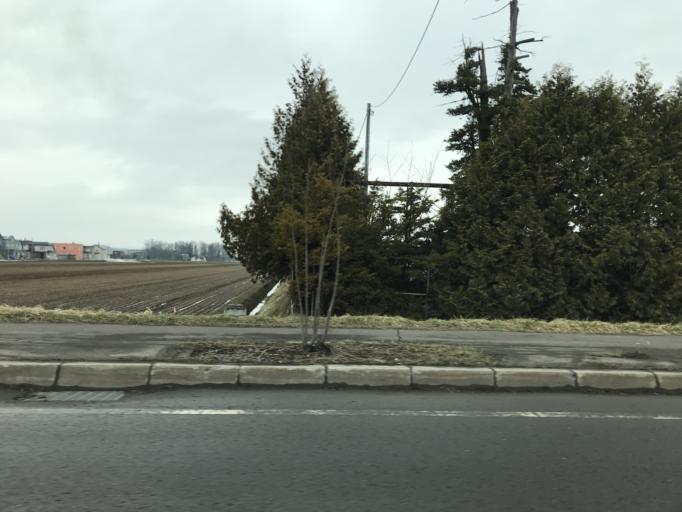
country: JP
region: Hokkaido
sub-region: Asahikawa-shi
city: Asahikawa
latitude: 43.8273
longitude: 142.4195
